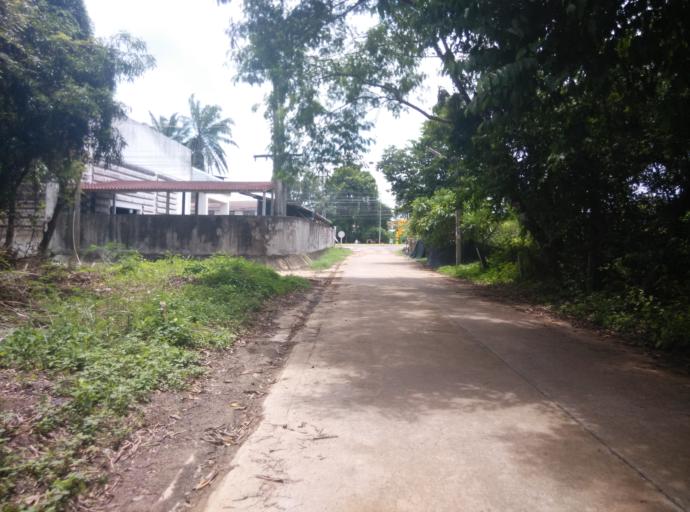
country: TH
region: Sisaket
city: Si Sa Ket
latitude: 15.1090
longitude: 104.3607
